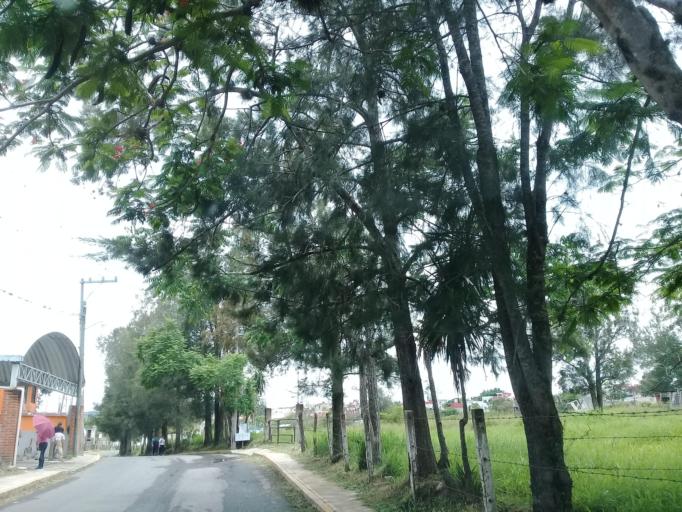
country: MX
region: Veracruz
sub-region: Emiliano Zapata
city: Dos Rios
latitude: 19.4642
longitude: -96.7844
